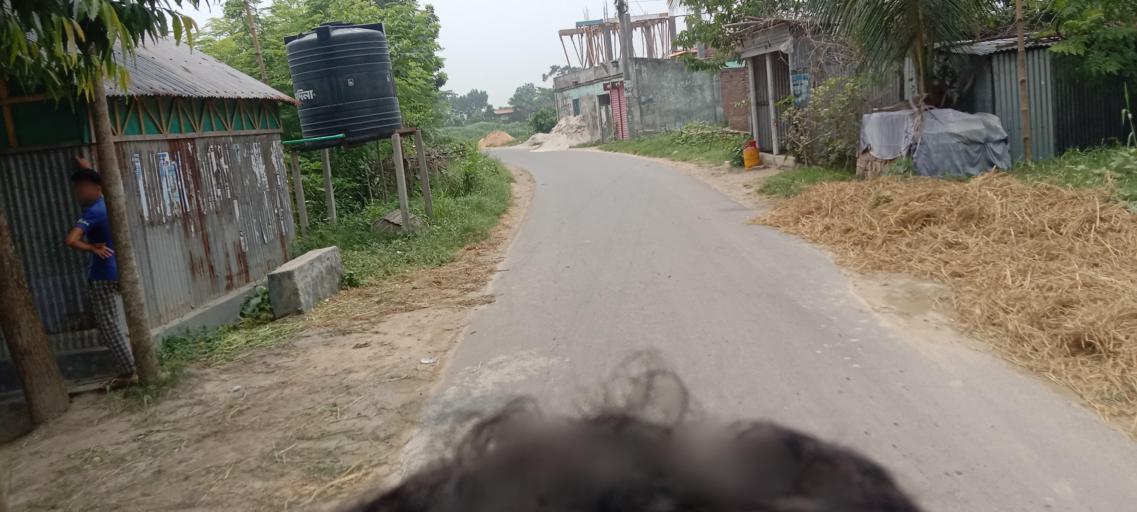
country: BD
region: Dhaka
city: Azimpur
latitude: 23.7465
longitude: 90.3021
